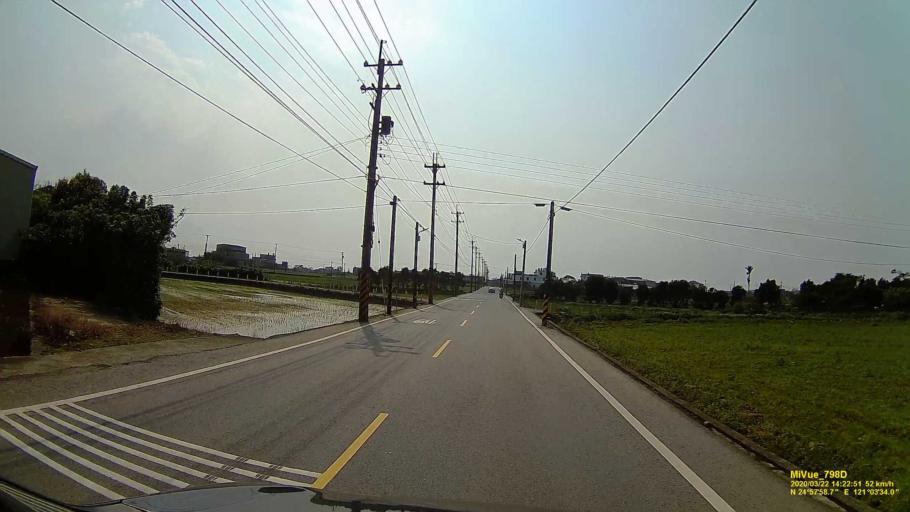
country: TW
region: Taiwan
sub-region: Hsinchu
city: Zhubei
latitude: 24.9663
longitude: 121.0592
